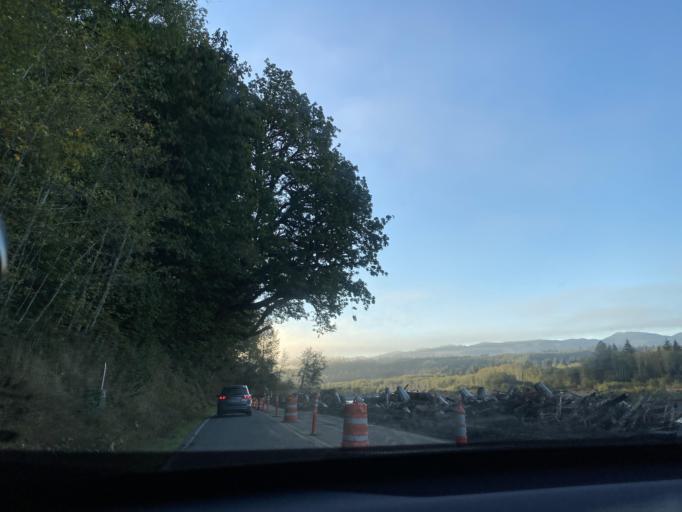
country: US
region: Washington
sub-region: Clallam County
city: Forks
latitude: 47.8219
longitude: -124.1821
